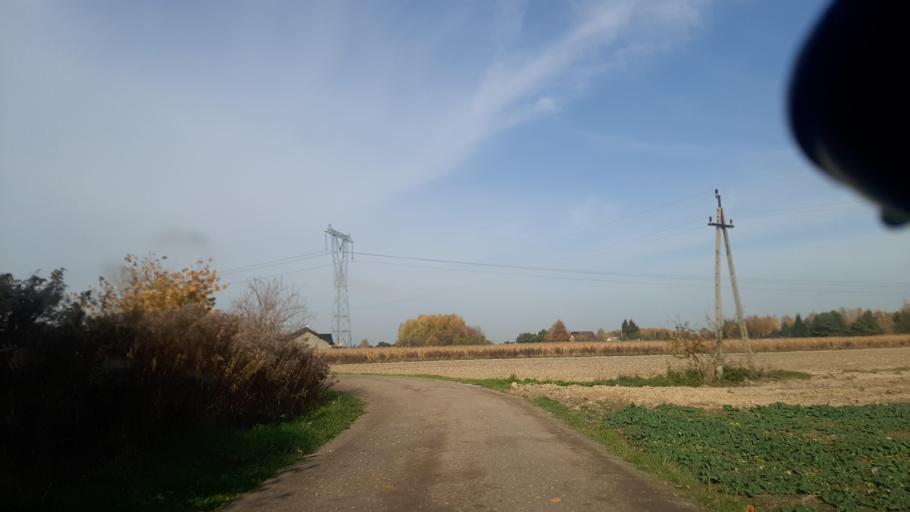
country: PL
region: Lublin Voivodeship
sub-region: Powiat lubelski
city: Lublin
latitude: 51.3311
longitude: 22.5439
